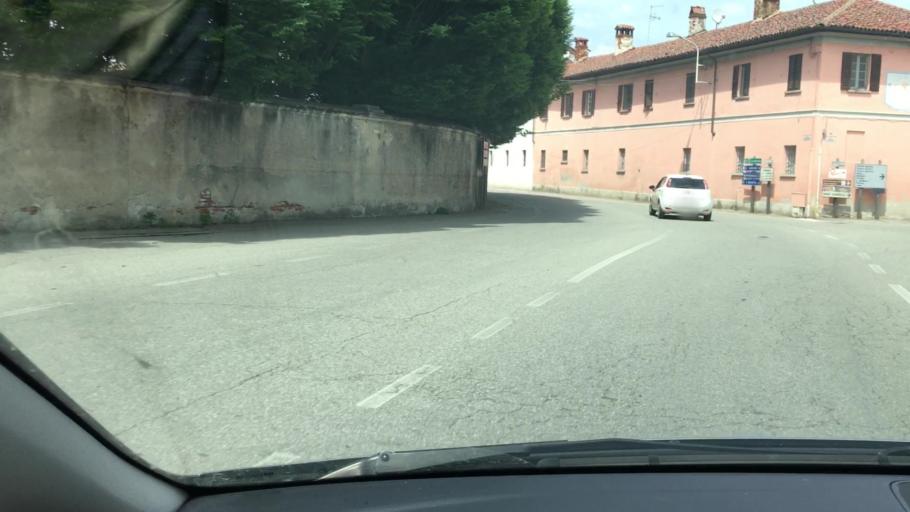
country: IT
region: Piedmont
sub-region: Provincia di Novara
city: Casalbeltrame
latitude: 45.4372
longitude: 8.4674
